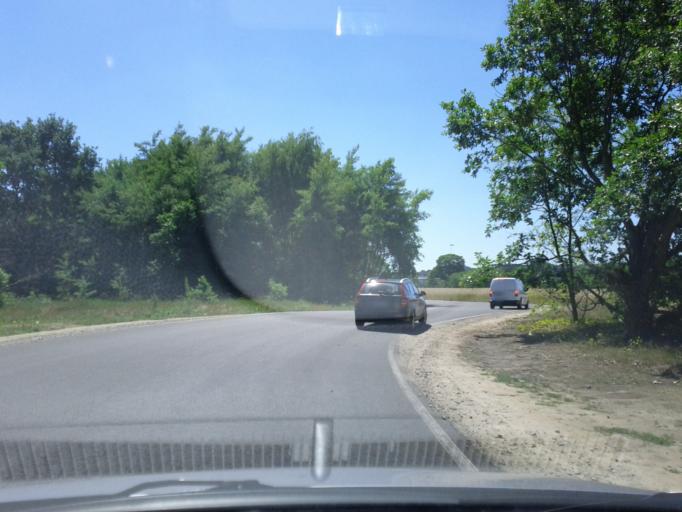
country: DE
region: Brandenburg
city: Langewahl
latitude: 52.3386
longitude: 14.0841
